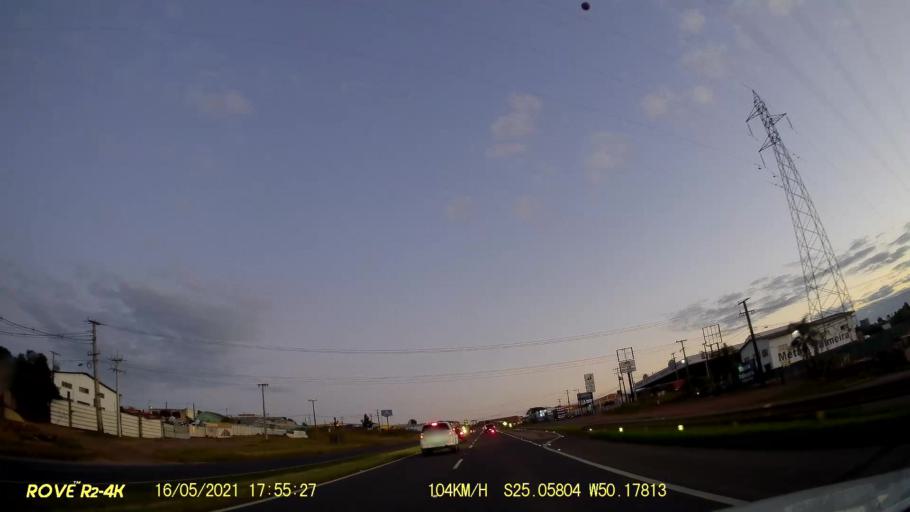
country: BR
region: Parana
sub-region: Ponta Grossa
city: Ponta Grossa
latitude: -25.0581
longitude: -50.1781
